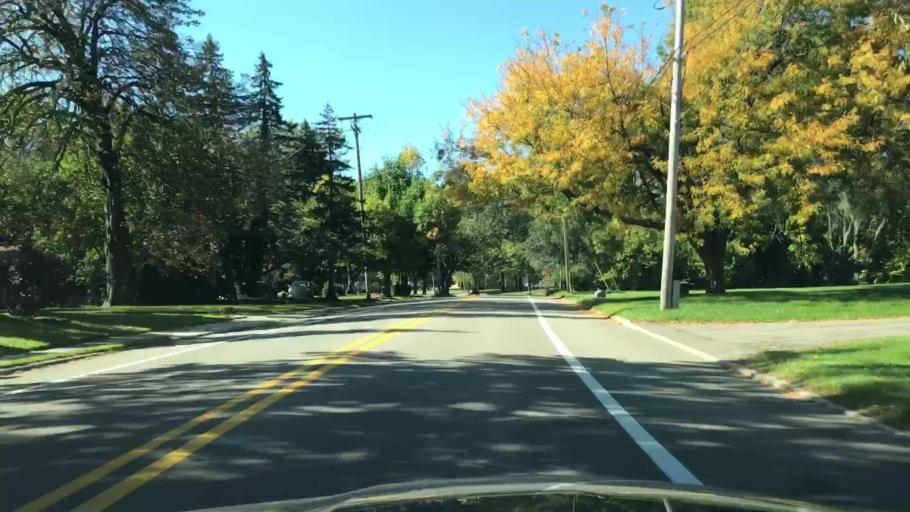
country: US
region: Michigan
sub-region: Macomb County
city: Center Line
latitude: 42.5273
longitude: -83.0528
